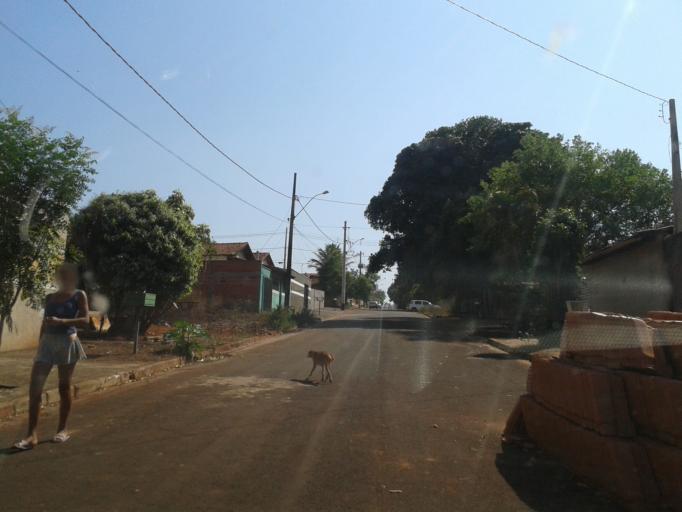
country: BR
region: Minas Gerais
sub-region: Ituiutaba
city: Ituiutaba
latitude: -18.9629
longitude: -49.4829
